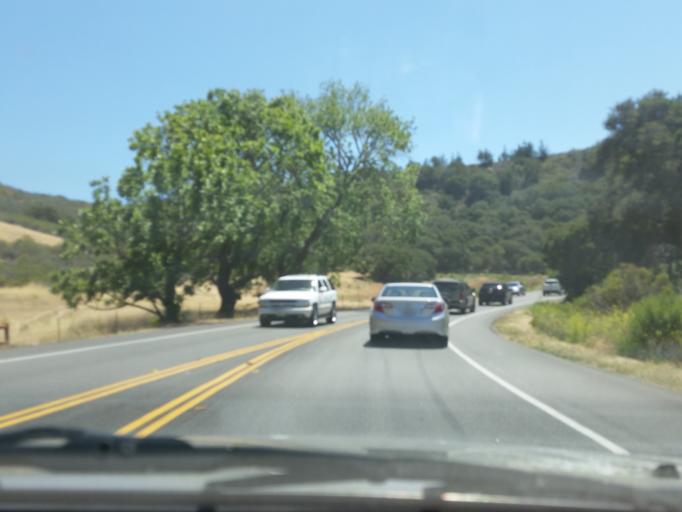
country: US
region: California
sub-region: San Luis Obispo County
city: Avila Beach
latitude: 35.1818
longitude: -120.7231
